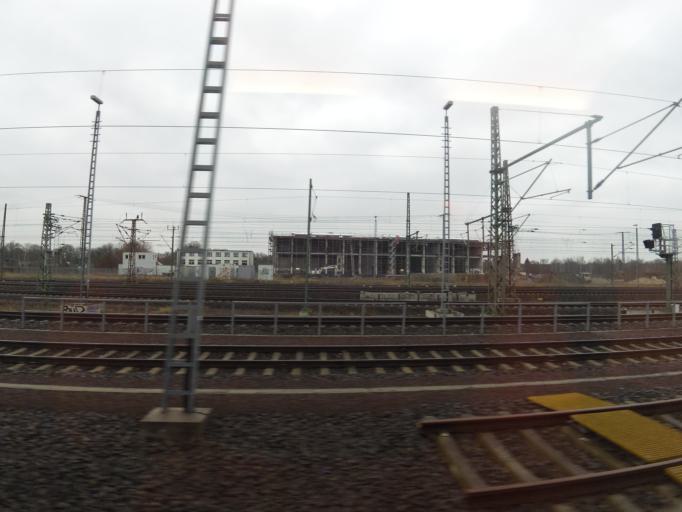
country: DE
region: Saxony-Anhalt
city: Magdeburg
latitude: 52.1245
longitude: 11.6253
